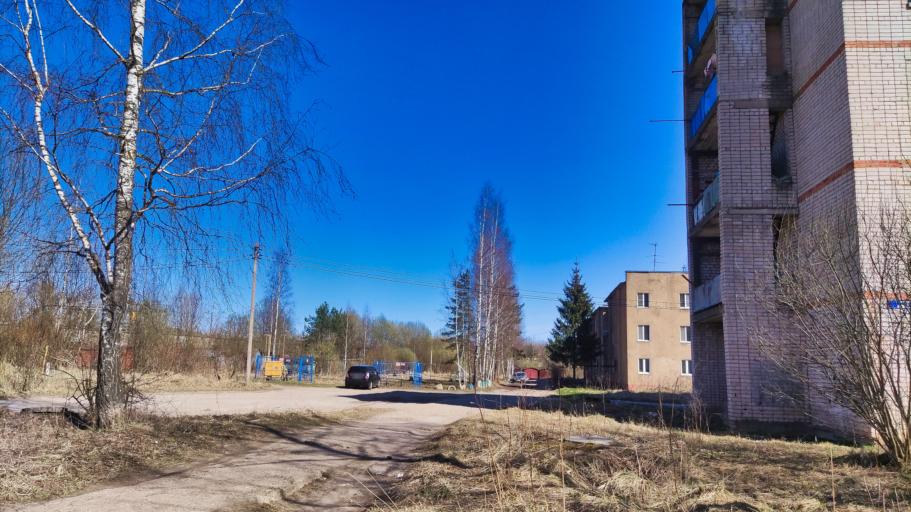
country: RU
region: Tverskaya
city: Rzhev
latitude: 56.2676
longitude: 34.2855
